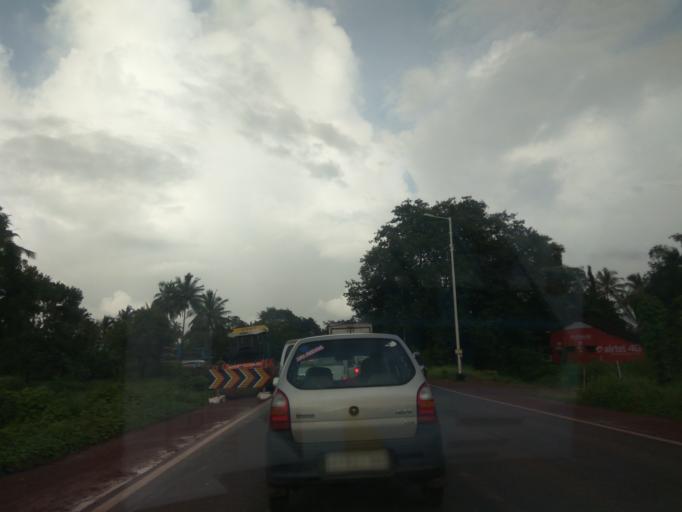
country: IN
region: Goa
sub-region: South Goa
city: Cortalim
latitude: 15.4237
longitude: 73.8987
